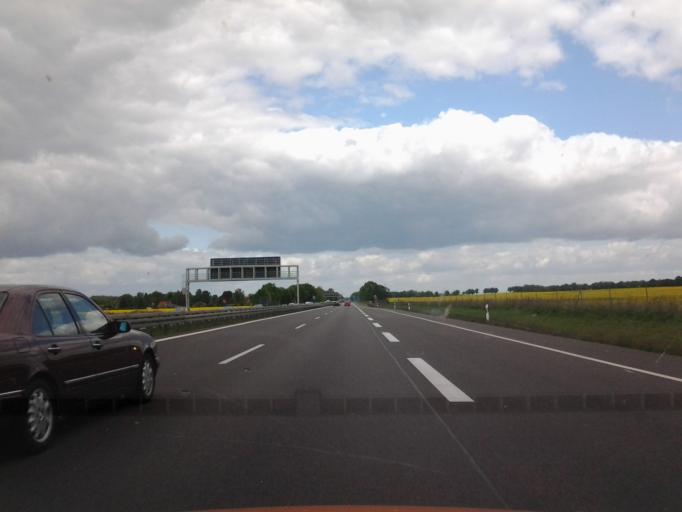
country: DE
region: Brandenburg
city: Bernau bei Berlin
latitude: 52.6304
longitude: 13.5652
